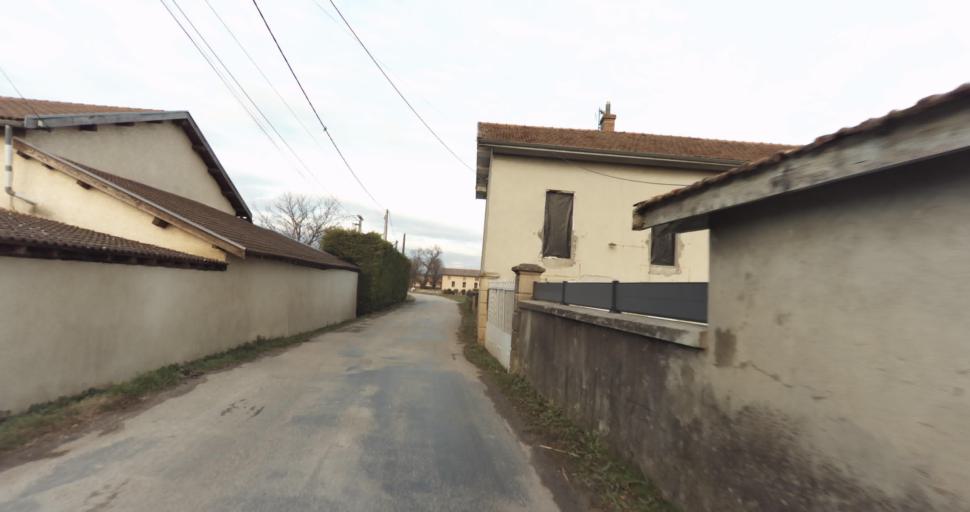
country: FR
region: Rhone-Alpes
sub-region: Departement de l'Isere
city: Allieres-et-Risset
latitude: 45.0765
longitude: 5.7010
